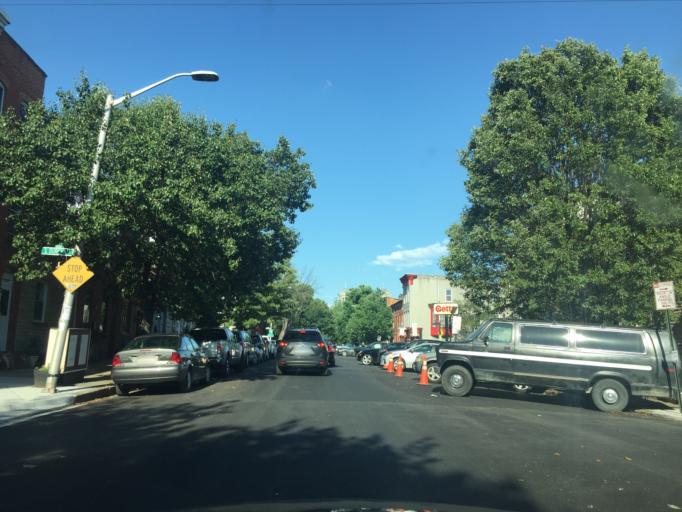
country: US
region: Maryland
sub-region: City of Baltimore
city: Baltimore
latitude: 39.2867
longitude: -76.5910
